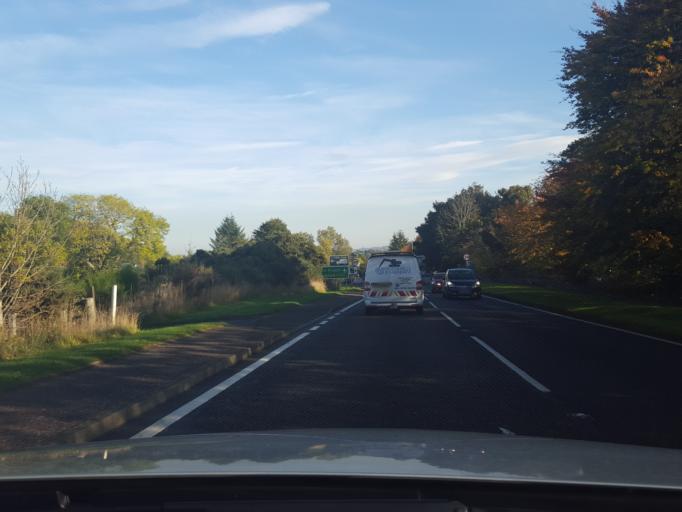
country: GB
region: Scotland
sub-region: Highland
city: Inverness
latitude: 57.4632
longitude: -4.2524
